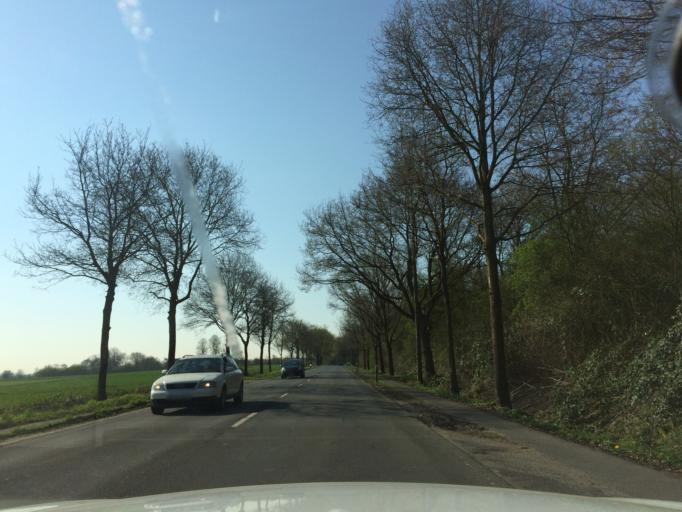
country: DE
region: North Rhine-Westphalia
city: Herten
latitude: 51.5955
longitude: 7.0954
